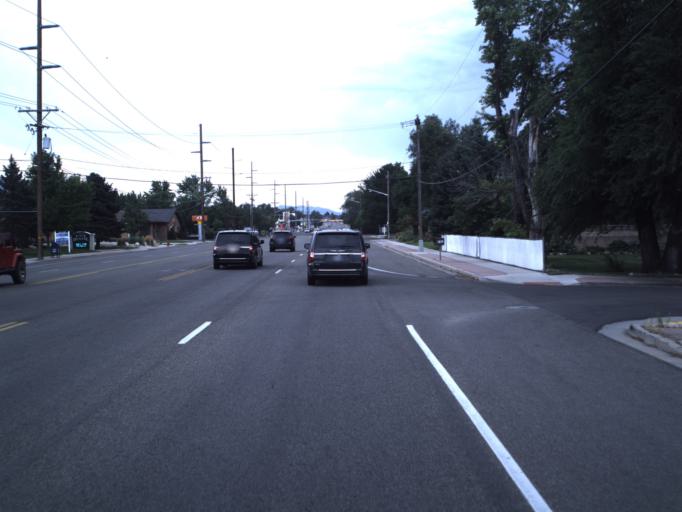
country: US
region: Utah
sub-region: Salt Lake County
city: Midvale
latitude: 40.6269
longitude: -111.8661
